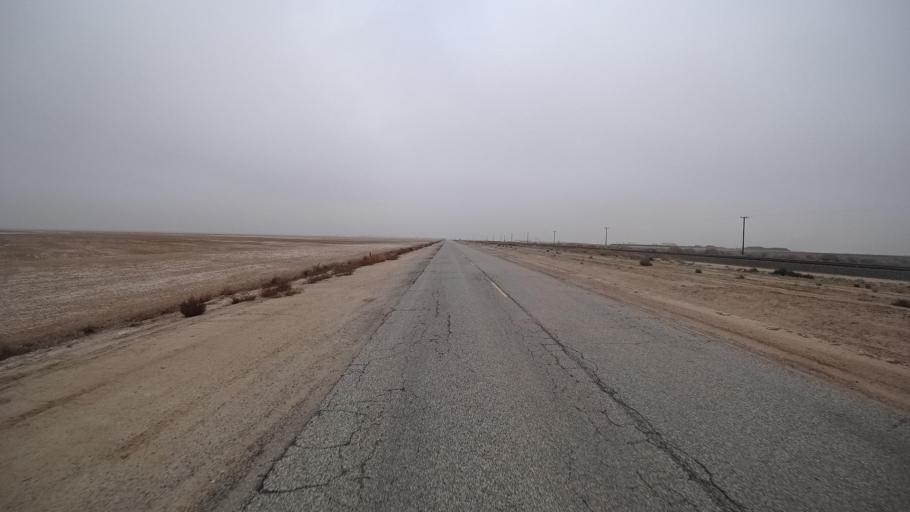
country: US
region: California
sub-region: Kern County
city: Maricopa
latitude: 35.1303
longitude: -119.2559
